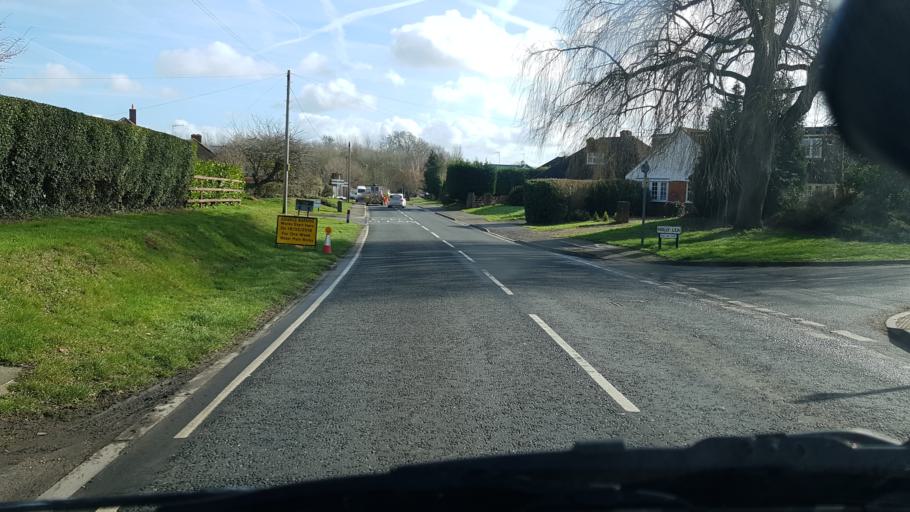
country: GB
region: England
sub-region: Surrey
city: Guildford
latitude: 51.2695
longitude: -0.5696
